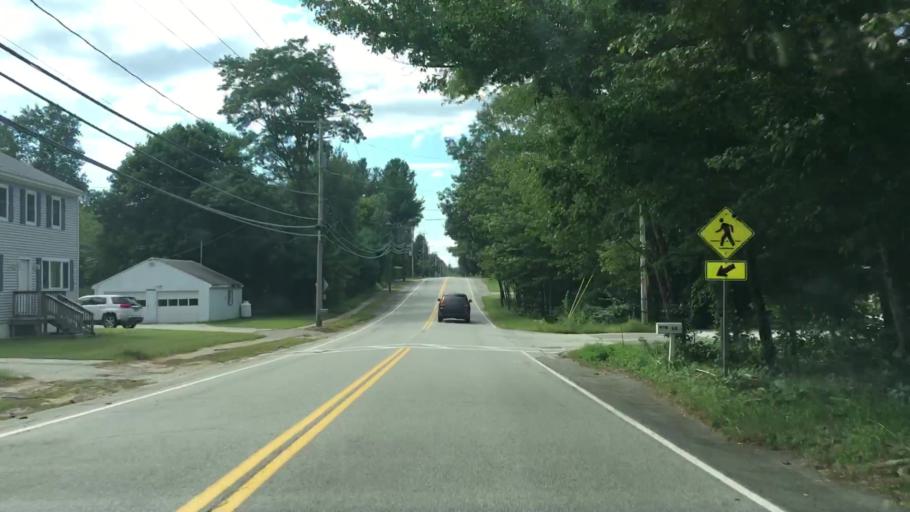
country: US
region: New Hampshire
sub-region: Strafford County
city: Somersworth
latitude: 43.2588
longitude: -70.8743
